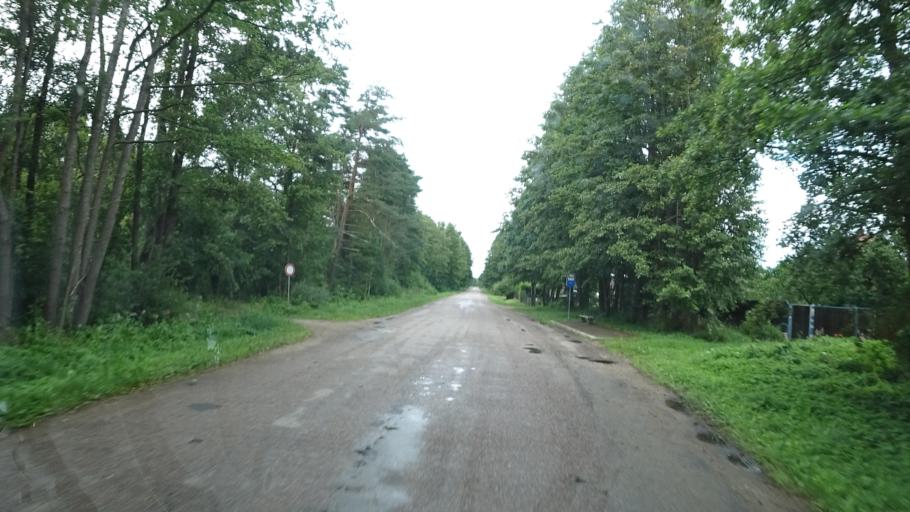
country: LV
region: Liepaja
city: Vec-Liepaja
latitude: 56.6120
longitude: 21.0388
